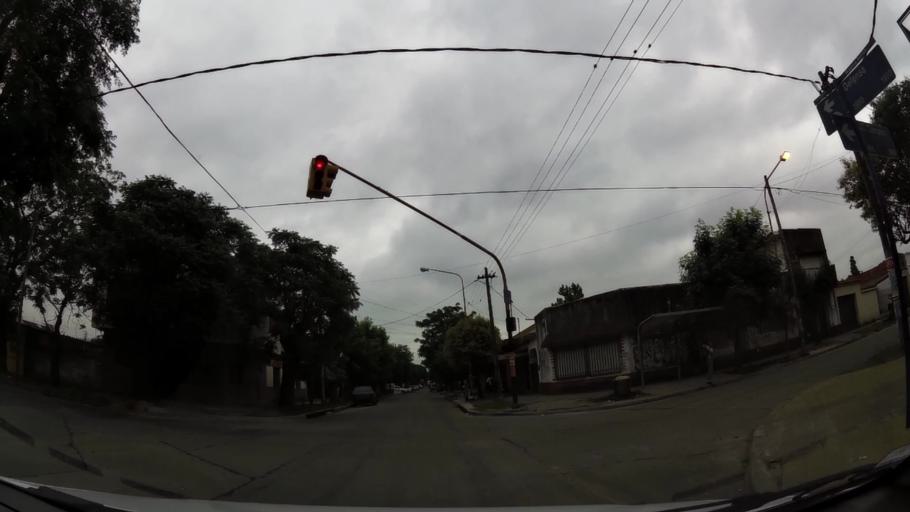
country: AR
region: Buenos Aires
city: San Justo
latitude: -34.7085
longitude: -58.5175
